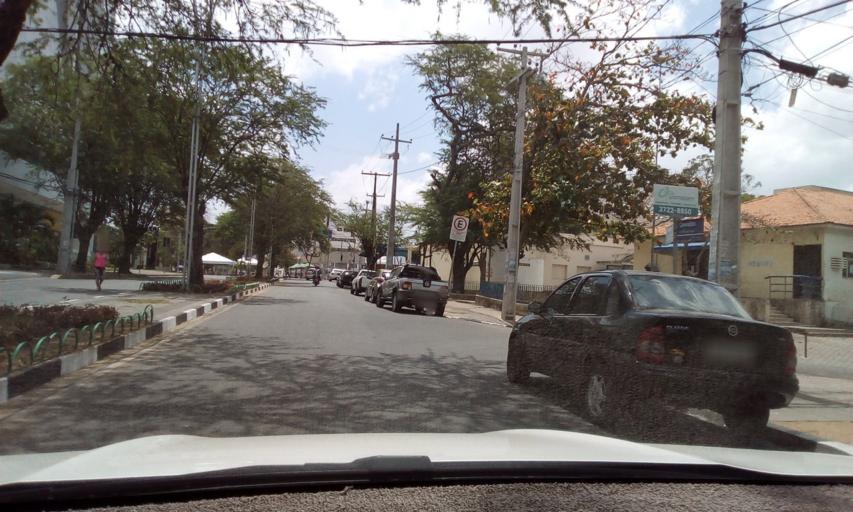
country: BR
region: Pernambuco
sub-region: Caruaru
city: Caruaru
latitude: -8.2803
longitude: -35.9704
